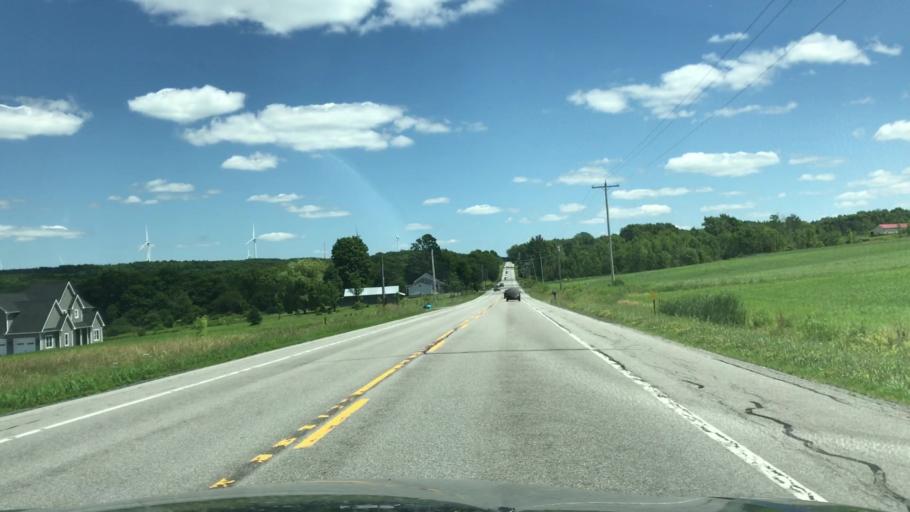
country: US
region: New York
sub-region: Wyoming County
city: Attica
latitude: 42.7540
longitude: -78.2681
